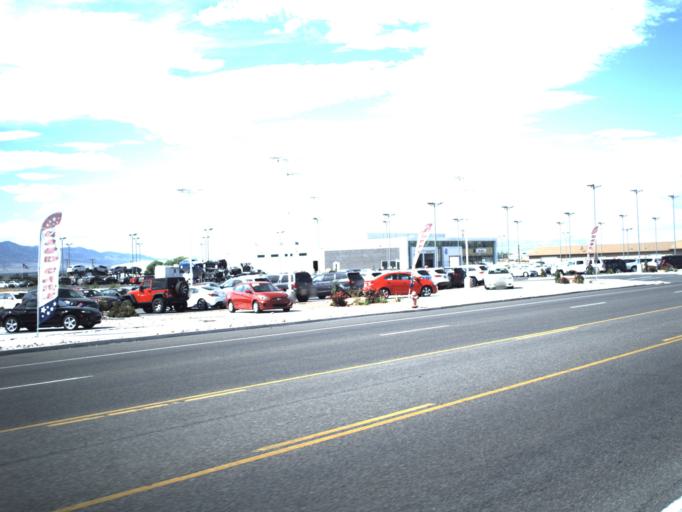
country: US
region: Utah
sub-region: Cache County
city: Hyde Park
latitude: 41.7893
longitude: -111.8336
